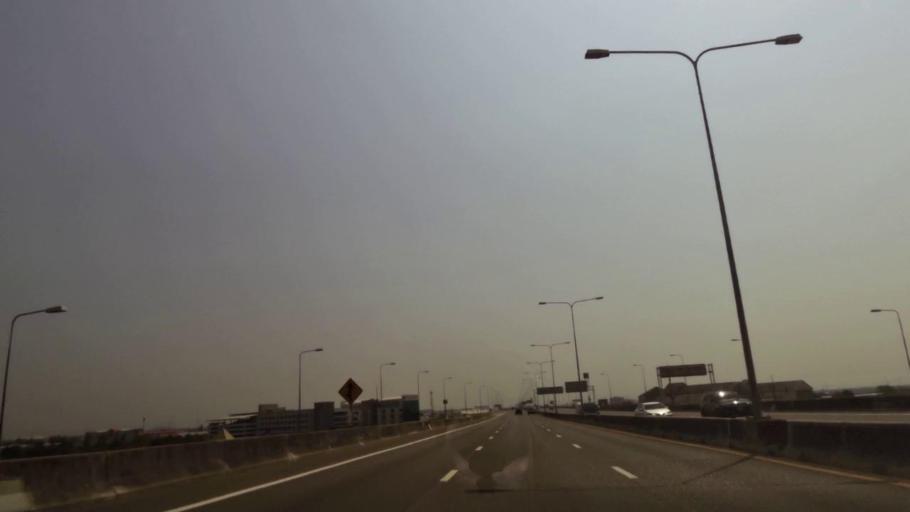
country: TH
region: Chachoengsao
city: Bang Pakong
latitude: 13.5452
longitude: 100.9614
